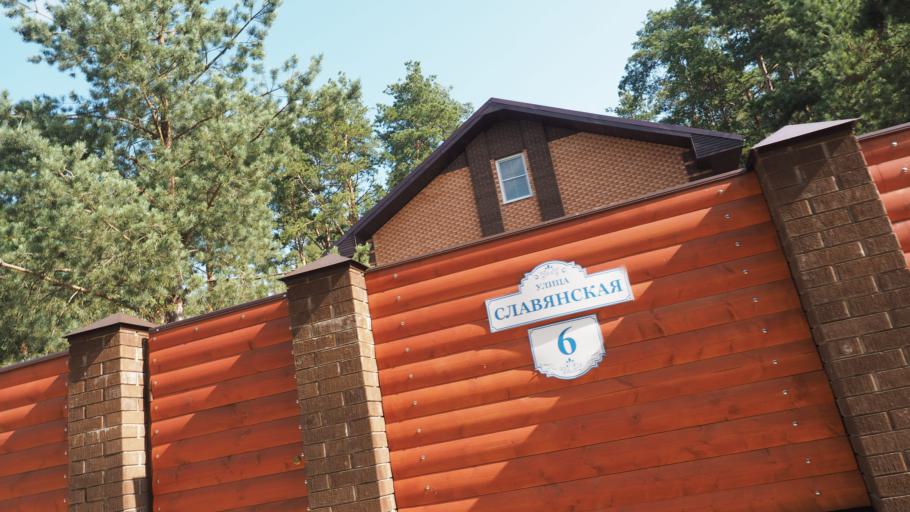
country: RU
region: Moskovskaya
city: Ramenskoye
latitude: 55.5901
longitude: 38.2914
